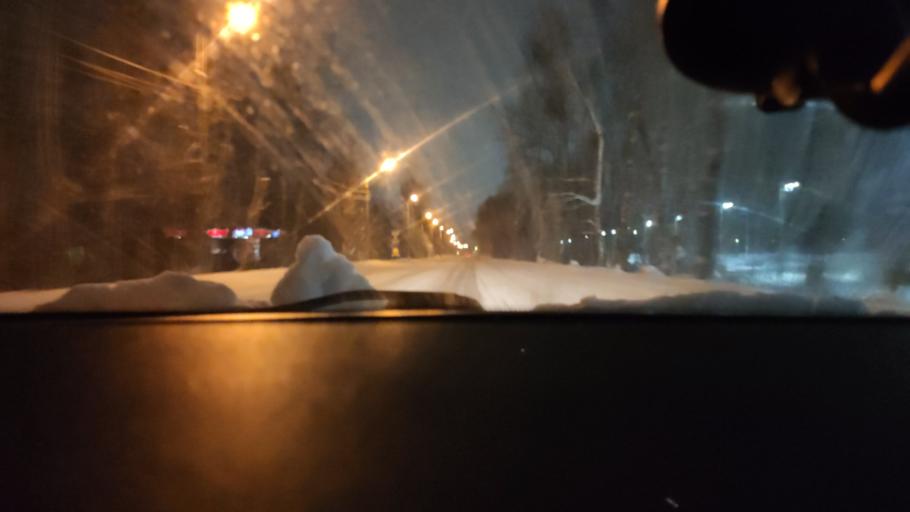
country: RU
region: Perm
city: Krasnokamsk
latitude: 58.0634
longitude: 55.8007
